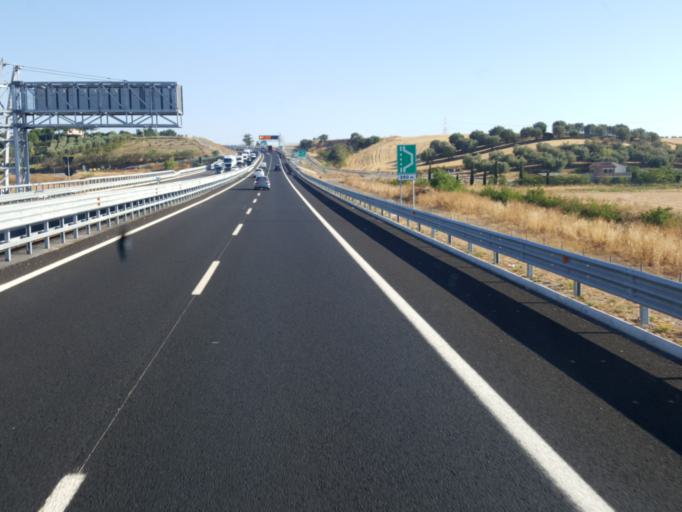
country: IT
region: Latium
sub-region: Citta metropolitana di Roma Capitale
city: Aurelia
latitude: 42.1920
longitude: 11.7862
